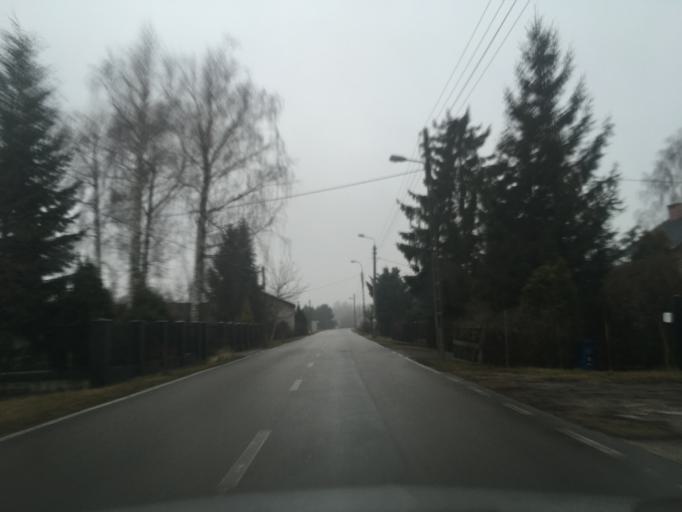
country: PL
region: Masovian Voivodeship
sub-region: Powiat piaseczynski
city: Lesznowola
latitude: 52.0573
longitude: 20.9079
